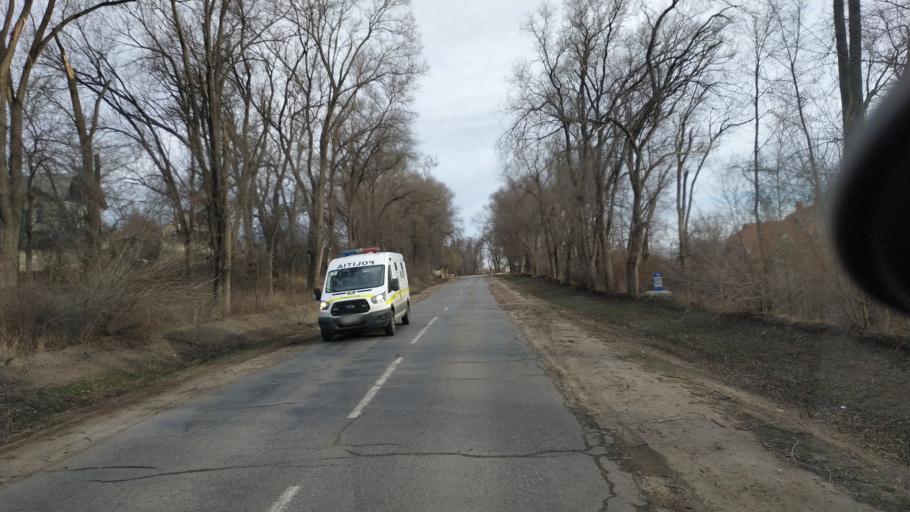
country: MD
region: Chisinau
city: Vadul lui Voda
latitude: 47.1198
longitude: 29.0635
